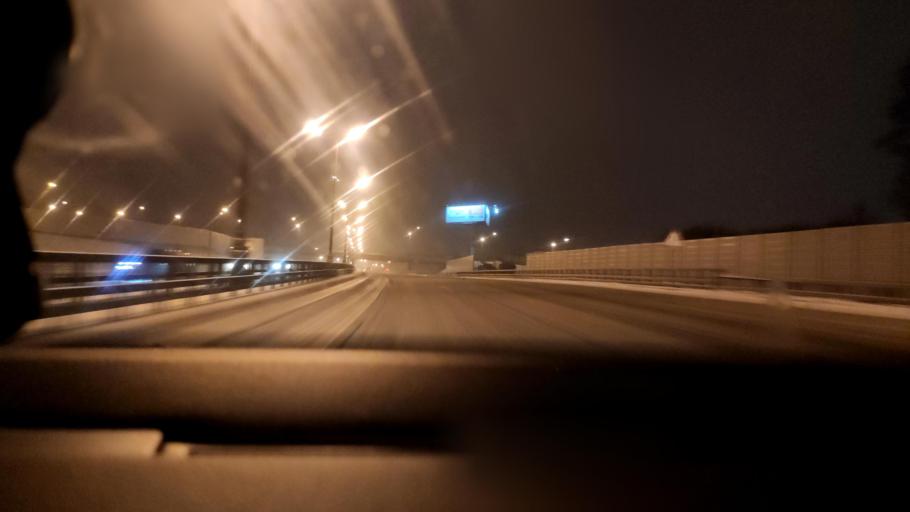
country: RU
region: Moskovskaya
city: Selyatino
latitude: 55.5183
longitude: 36.9980
